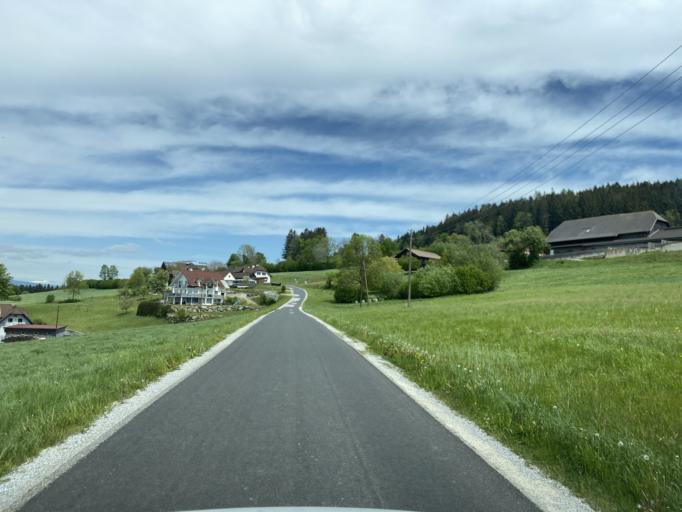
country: AT
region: Styria
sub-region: Politischer Bezirk Weiz
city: Gschaid bei Birkfeld
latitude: 47.3526
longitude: 15.7211
